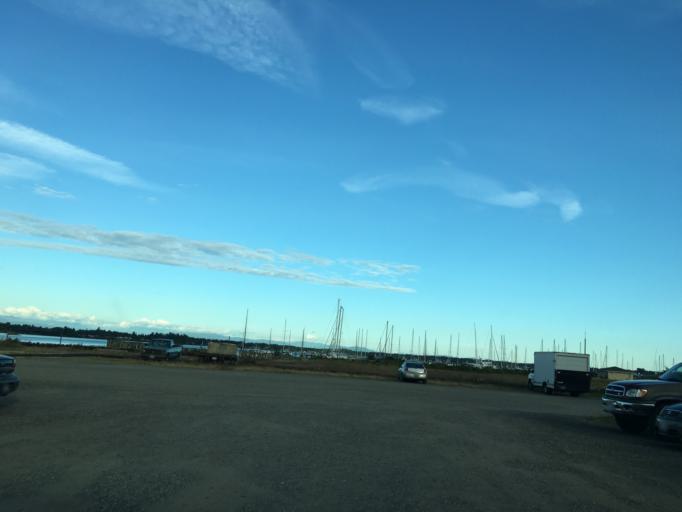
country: US
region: Washington
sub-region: Whatcom County
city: Blaine
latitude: 48.9905
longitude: -122.7723
